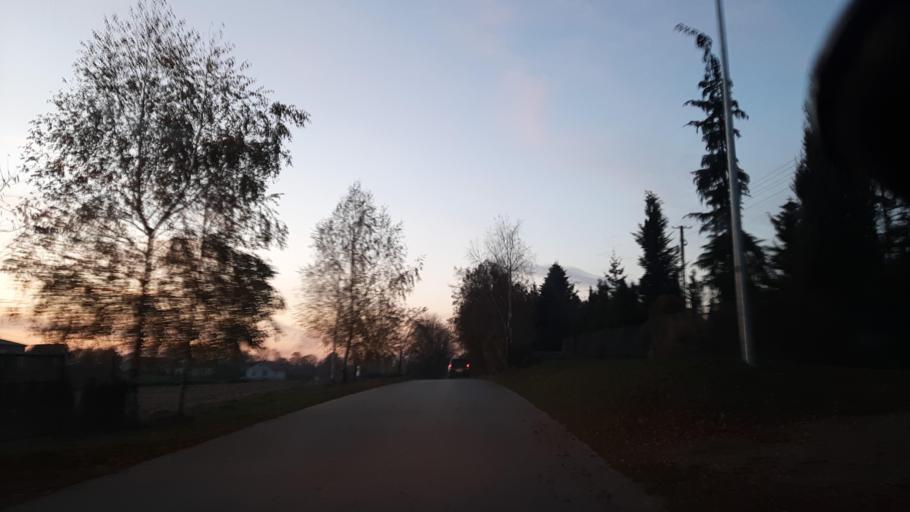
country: PL
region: Lublin Voivodeship
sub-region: Powiat lubelski
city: Jastkow
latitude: 51.3381
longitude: 22.4238
